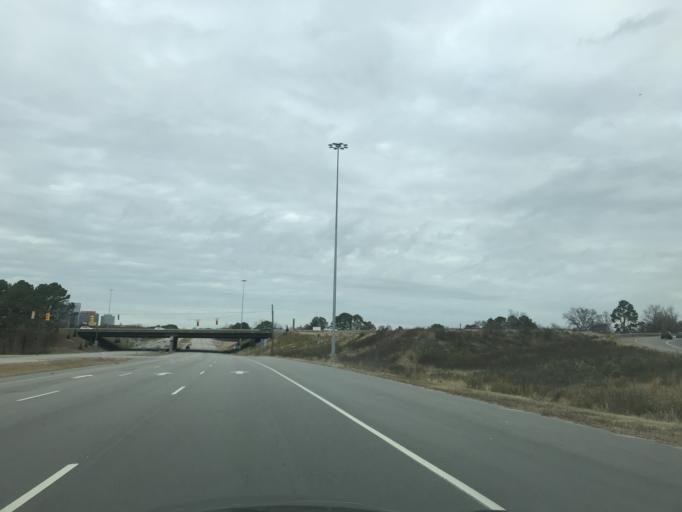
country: US
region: North Carolina
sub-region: Wake County
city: Raleigh
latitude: 35.7515
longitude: -78.6358
